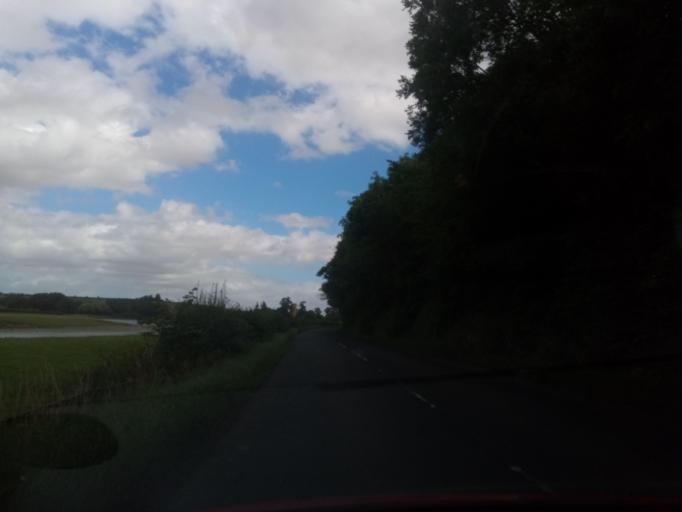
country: GB
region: Scotland
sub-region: The Scottish Borders
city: Coldstream
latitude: 55.6350
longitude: -2.3273
